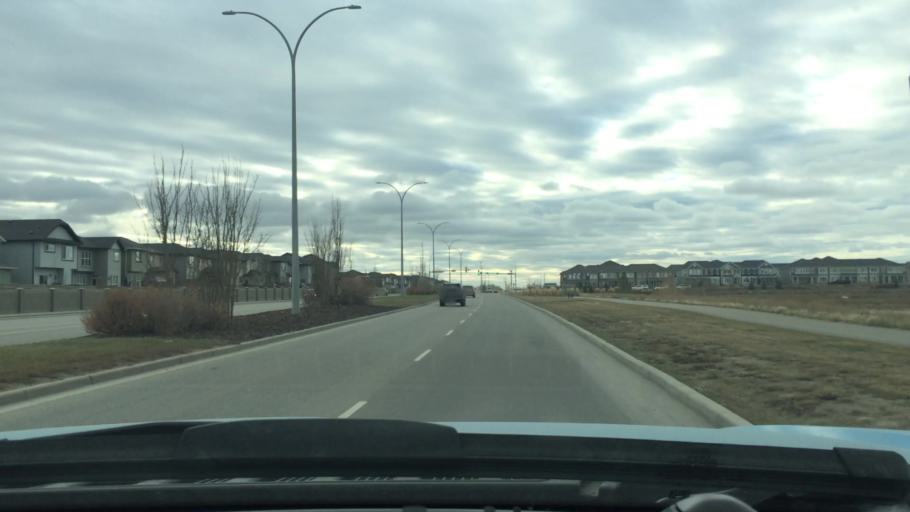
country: CA
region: Alberta
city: Airdrie
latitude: 51.2556
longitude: -114.0252
